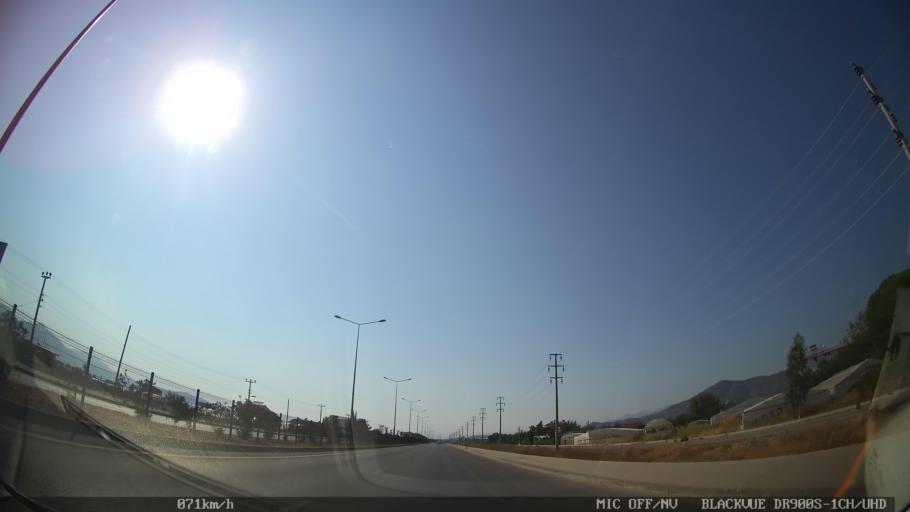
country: TR
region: Mugla
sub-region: Fethiye
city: Fethiye
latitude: 36.6534
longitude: 29.1712
